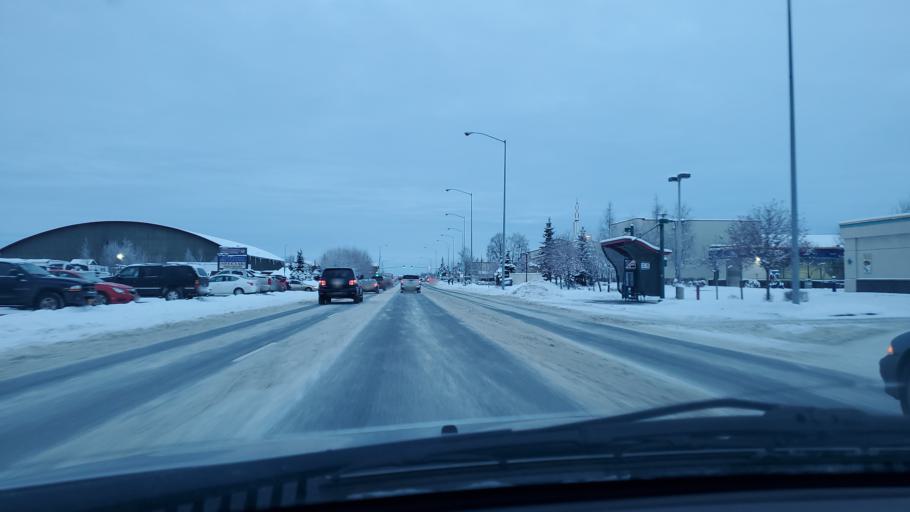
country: US
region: Alaska
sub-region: Anchorage Municipality
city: Anchorage
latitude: 61.1955
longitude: -149.8831
